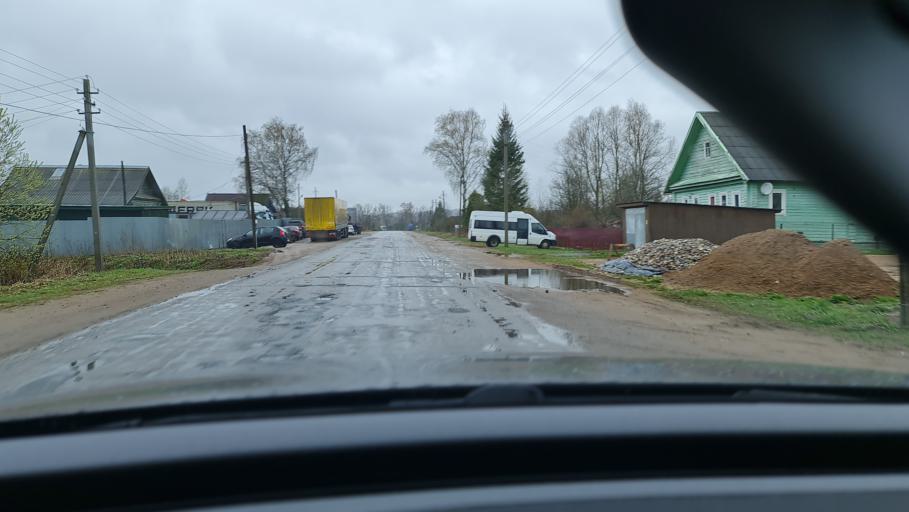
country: RU
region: Novgorod
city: Valday
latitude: 58.0335
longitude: 32.9669
